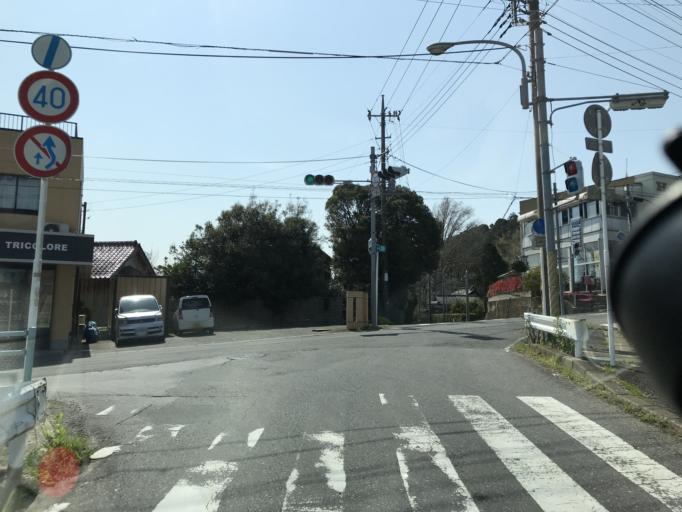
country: JP
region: Chiba
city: Yokaichiba
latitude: 35.7542
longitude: 140.5851
